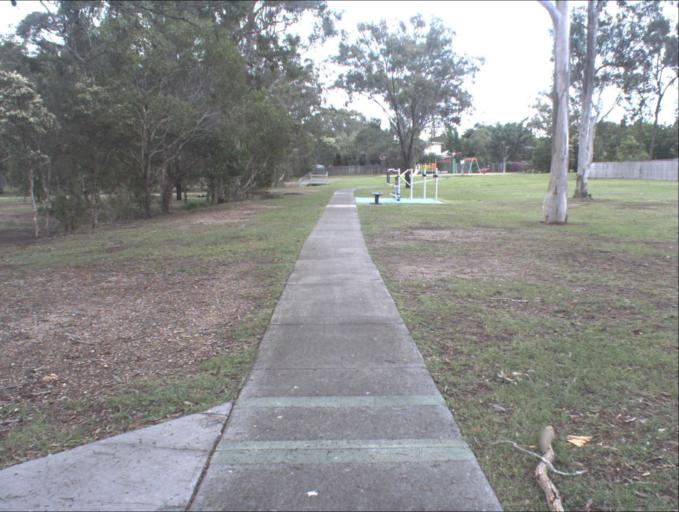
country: AU
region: Queensland
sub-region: Logan
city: Waterford West
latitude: -27.6885
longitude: 153.1187
